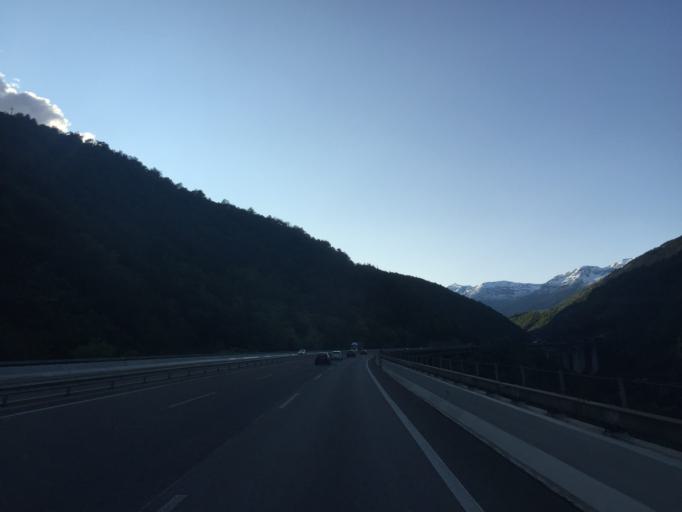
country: CH
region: Ticino
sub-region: Leventina District
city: Bodio
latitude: 46.4131
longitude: 8.8623
